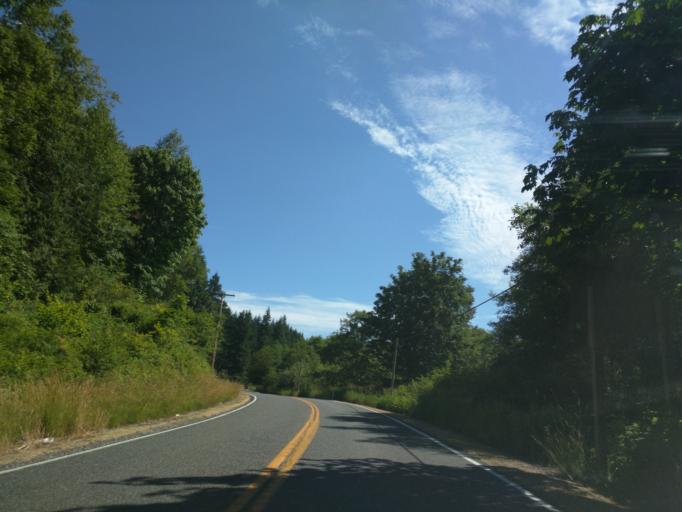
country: US
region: Washington
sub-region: Whatcom County
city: Sumas
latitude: 48.9638
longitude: -122.2236
